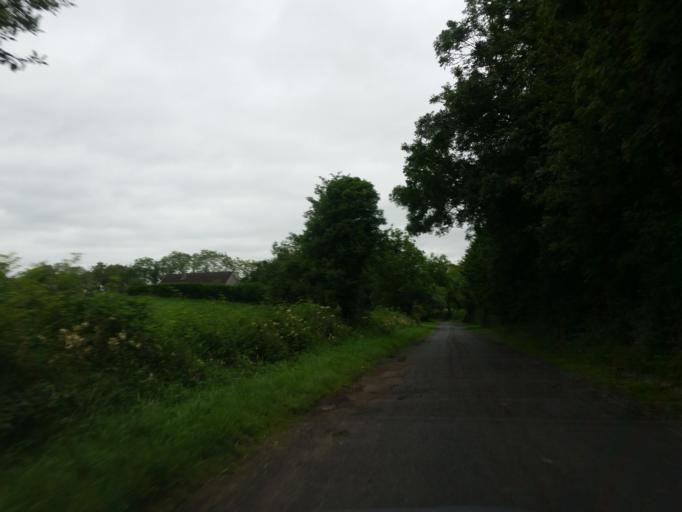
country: GB
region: Northern Ireland
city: Lisnaskea
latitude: 54.3101
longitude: -7.4940
